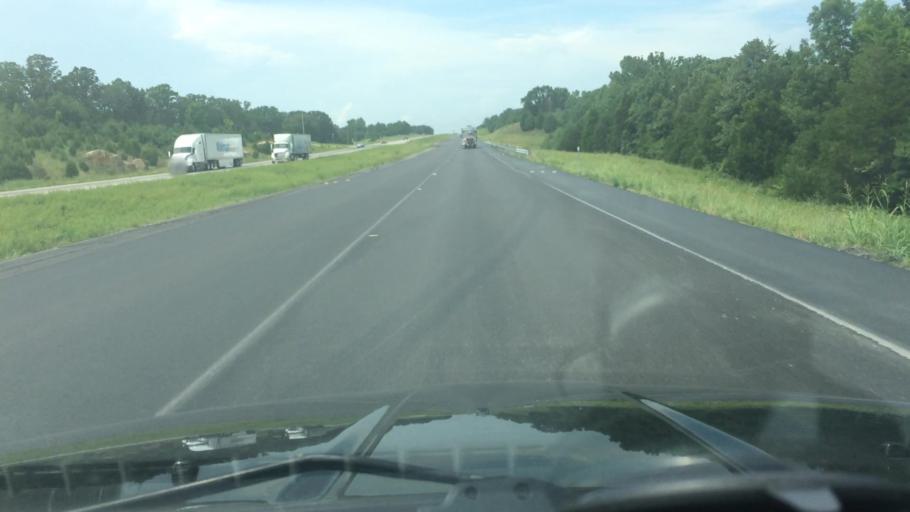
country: US
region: Missouri
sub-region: Saint Clair County
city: Osceola
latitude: 37.9581
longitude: -93.6426
